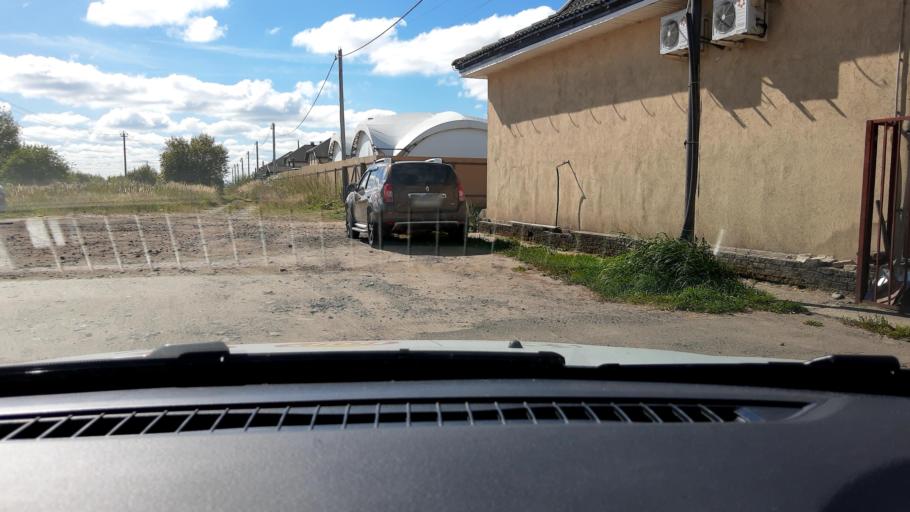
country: RU
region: Nizjnij Novgorod
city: Babino
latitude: 56.1326
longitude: 43.6426
